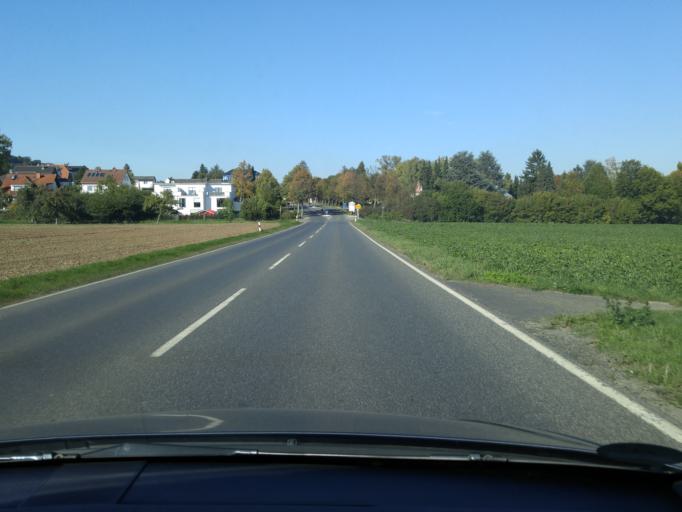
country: DE
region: Hesse
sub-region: Regierungsbezirk Darmstadt
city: Bad Nauheim
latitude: 50.3525
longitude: 8.7348
